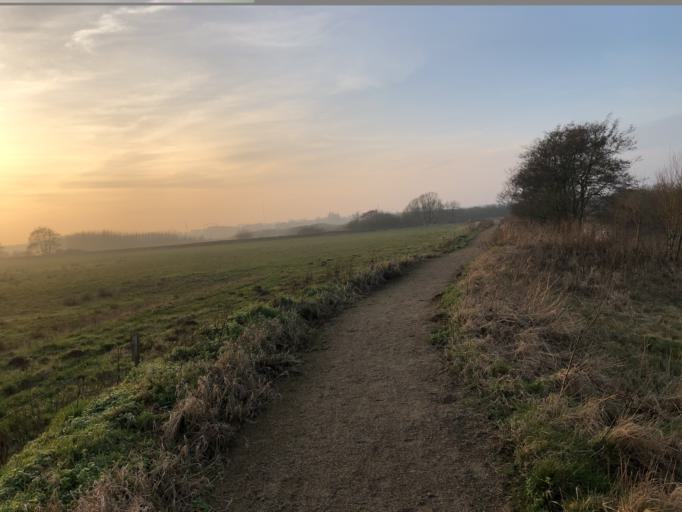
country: DK
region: Central Jutland
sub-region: Holstebro Kommune
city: Ulfborg
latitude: 56.3425
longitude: 8.3659
